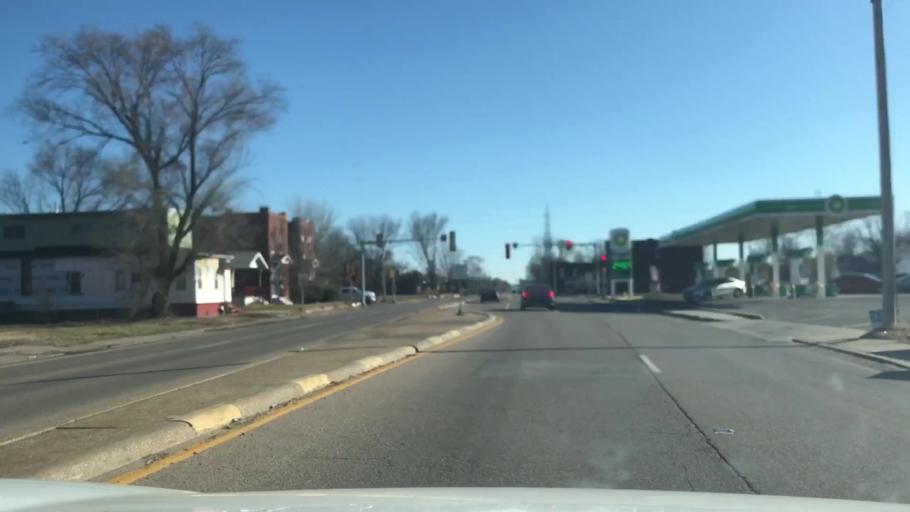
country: US
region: Illinois
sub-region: Saint Clair County
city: East Saint Louis
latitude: 38.6135
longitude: -90.1440
